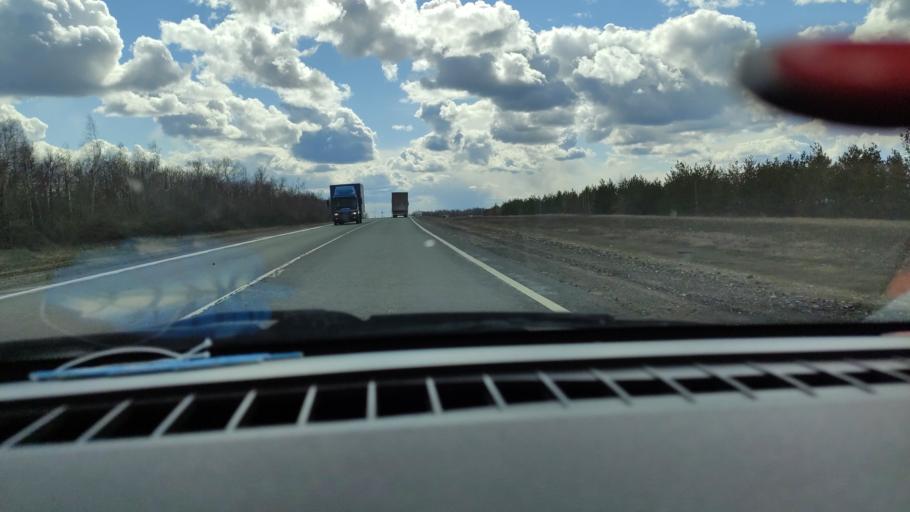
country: RU
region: Samara
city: Syzran'
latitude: 52.8692
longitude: 48.2817
